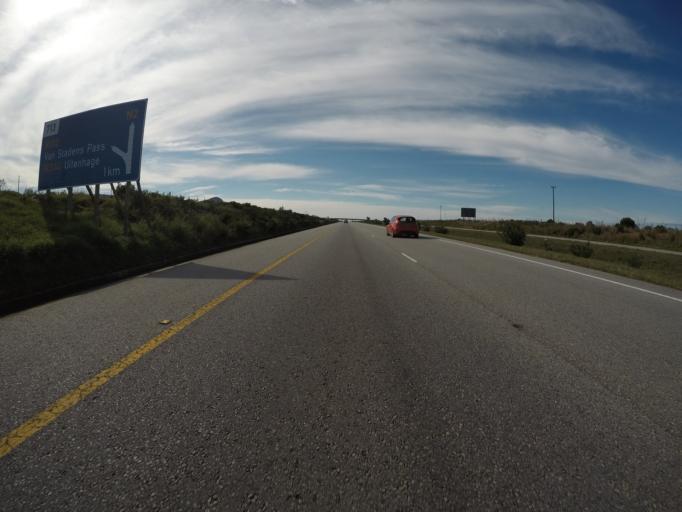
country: ZA
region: Eastern Cape
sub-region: Nelson Mandela Bay Metropolitan Municipality
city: Uitenhage
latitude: -33.9101
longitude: 25.2128
